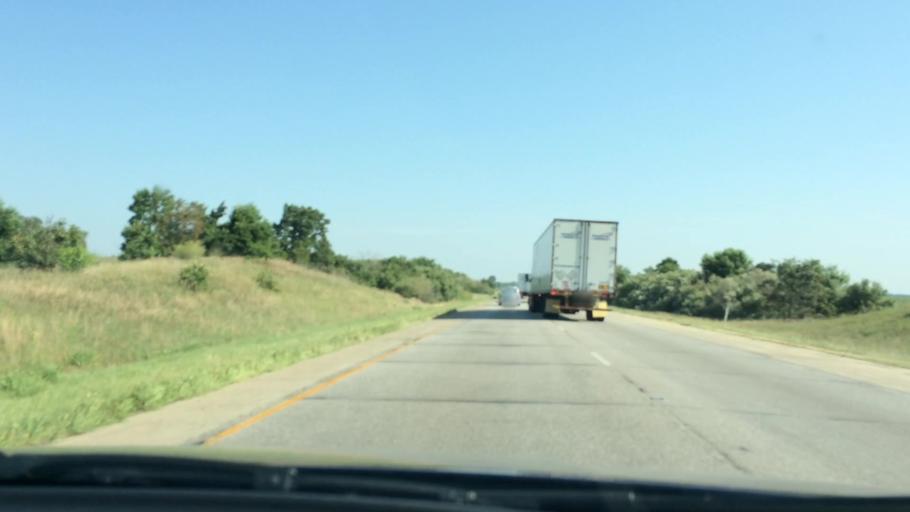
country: US
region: Indiana
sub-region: Newton County
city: Roselawn
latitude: 41.0457
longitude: -87.2703
